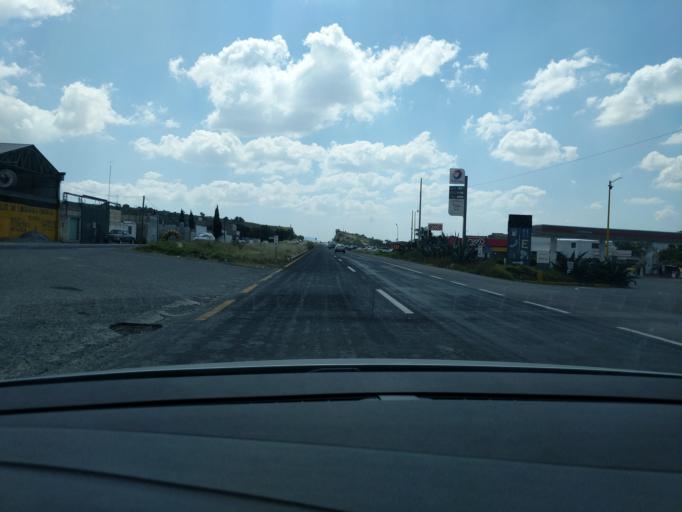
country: MX
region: Hidalgo
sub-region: Mineral de la Reforma
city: Rinconada de los Angeles
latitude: 19.9908
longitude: -98.7062
